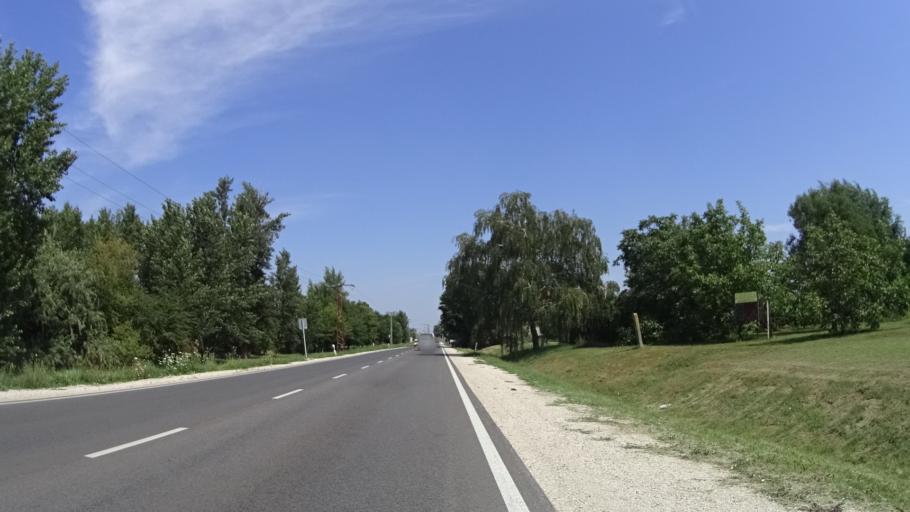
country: HU
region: Fejer
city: Szekesfehervar
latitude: 47.1564
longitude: 18.3998
